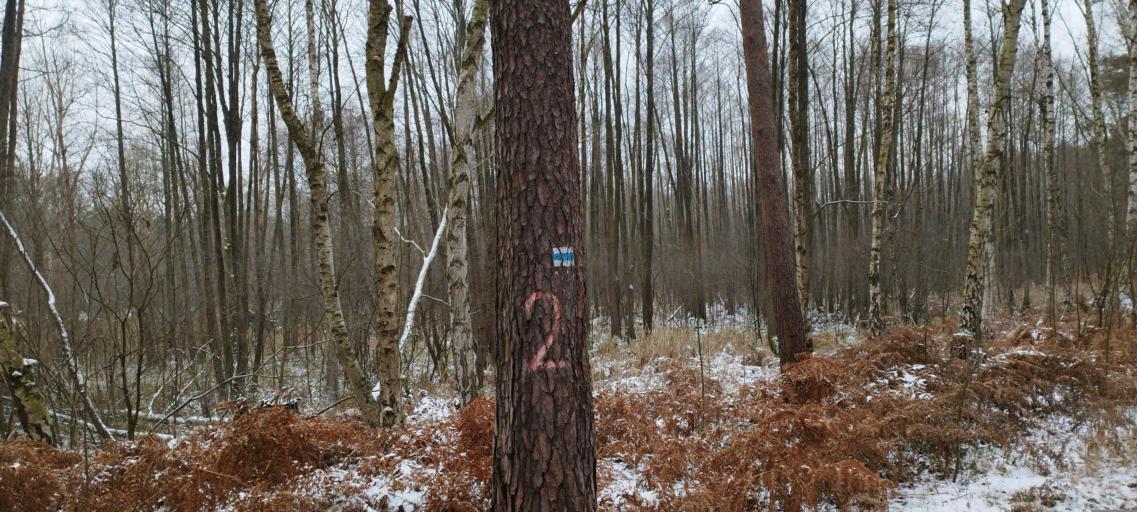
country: DE
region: Brandenburg
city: Halbe
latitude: 52.1479
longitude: 13.7570
